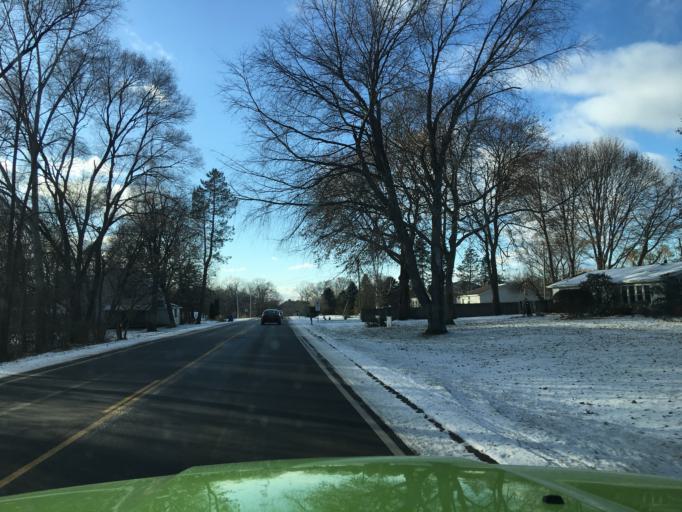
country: US
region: Michigan
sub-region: Montcalm County
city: Greenville
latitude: 43.2064
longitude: -85.2622
